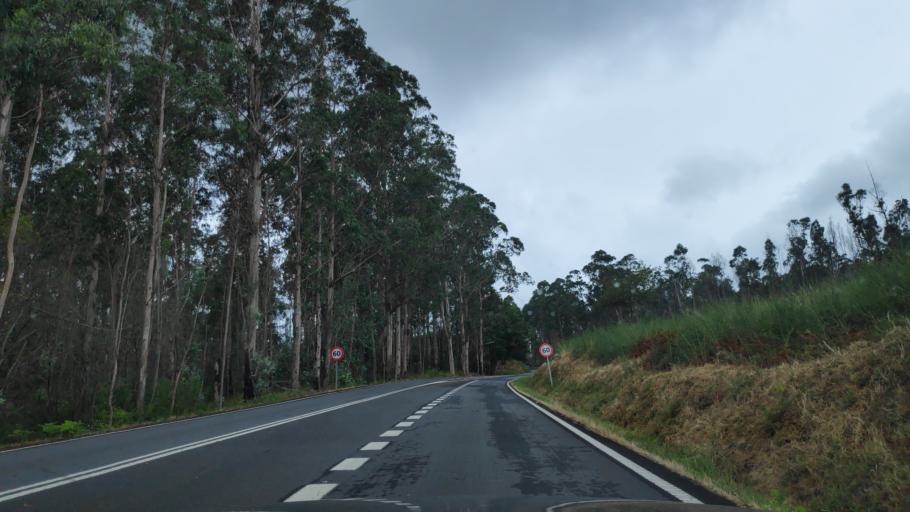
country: ES
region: Galicia
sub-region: Provincia de Pontevedra
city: Catoira
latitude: 42.6962
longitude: -8.7515
